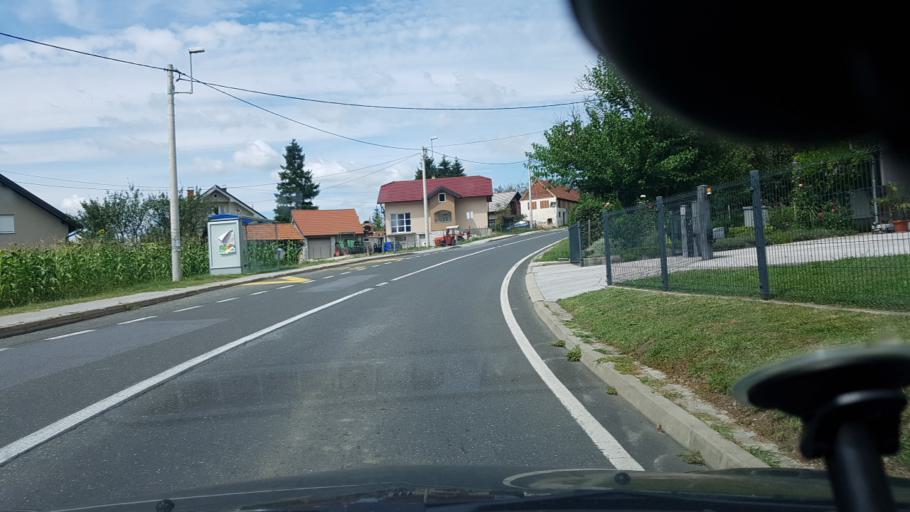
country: HR
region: Varazdinska
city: Lepoglava
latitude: 46.2079
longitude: 16.0214
